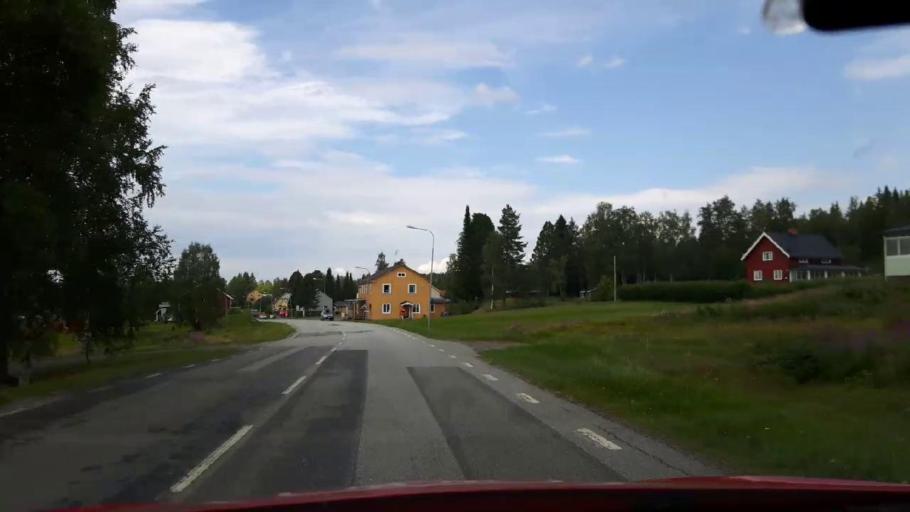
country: SE
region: Jaemtland
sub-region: Stroemsunds Kommun
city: Stroemsund
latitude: 64.4333
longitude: 15.5952
